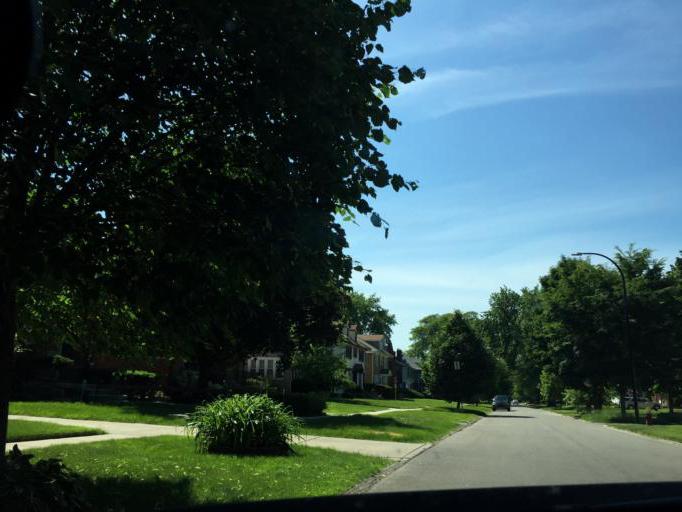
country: US
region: Michigan
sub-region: Oakland County
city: Southfield
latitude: 42.4061
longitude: -83.2293
